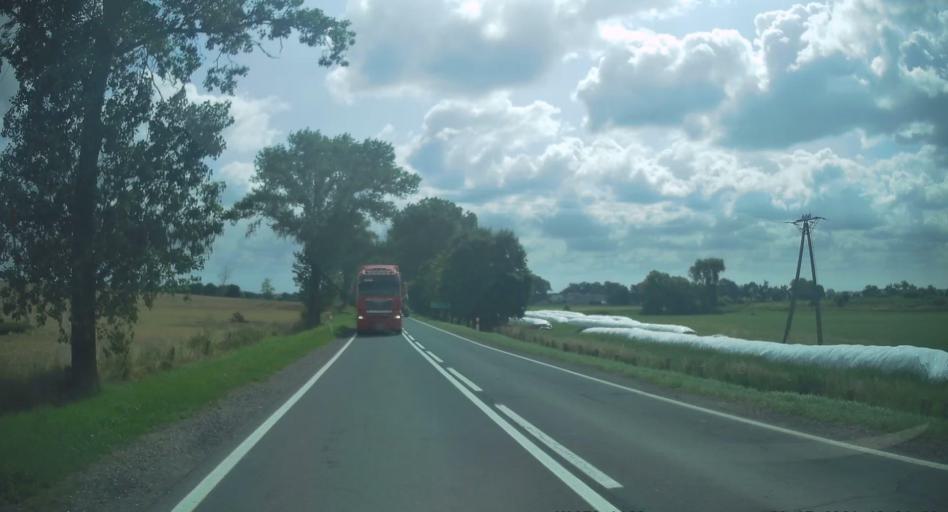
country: PL
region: Opole Voivodeship
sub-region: Powiat prudnicki
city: Twardawa
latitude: 50.3407
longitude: 17.9491
